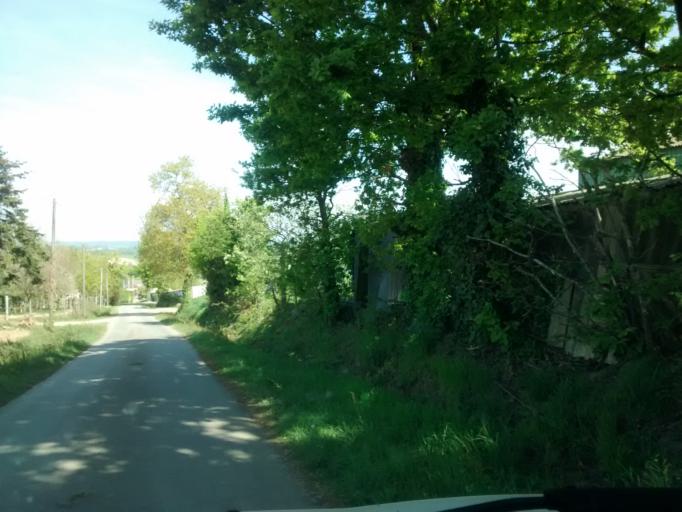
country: FR
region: Brittany
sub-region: Departement d'Ille-et-Vilaine
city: Messac
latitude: 47.7826
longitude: -1.7663
